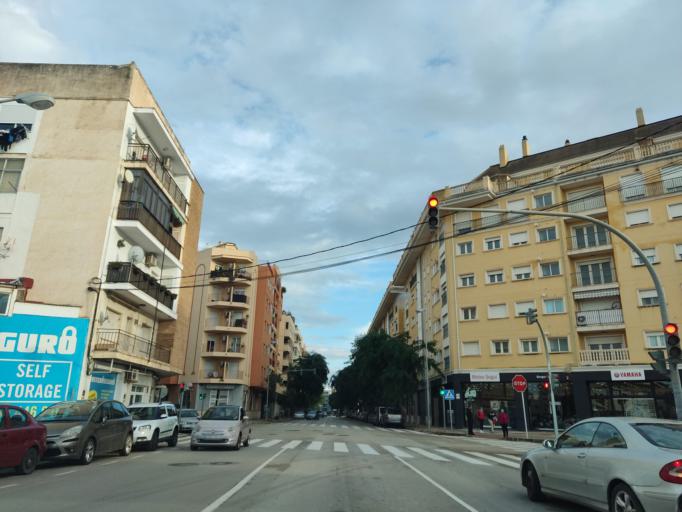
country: ES
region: Valencia
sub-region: Provincia de Alicante
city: Denia
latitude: 38.8386
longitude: 0.0986
